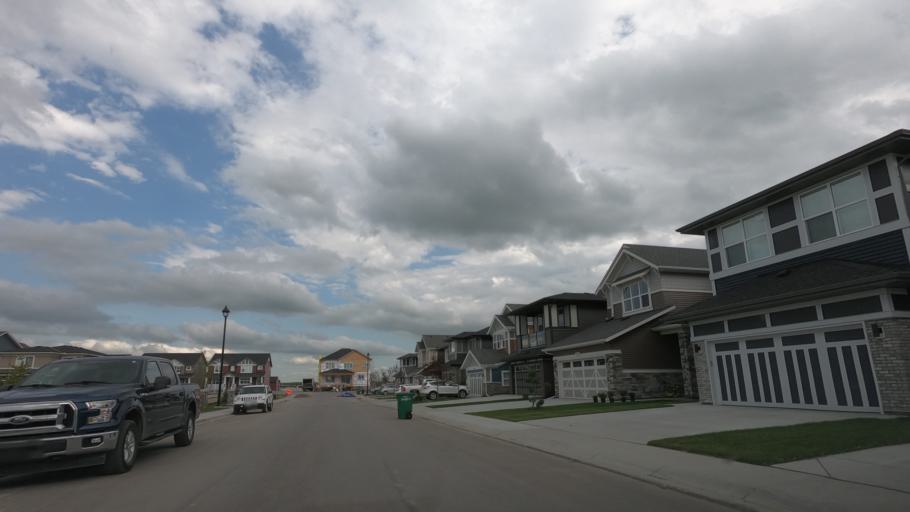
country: CA
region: Alberta
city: Airdrie
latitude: 51.2568
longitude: -113.9845
